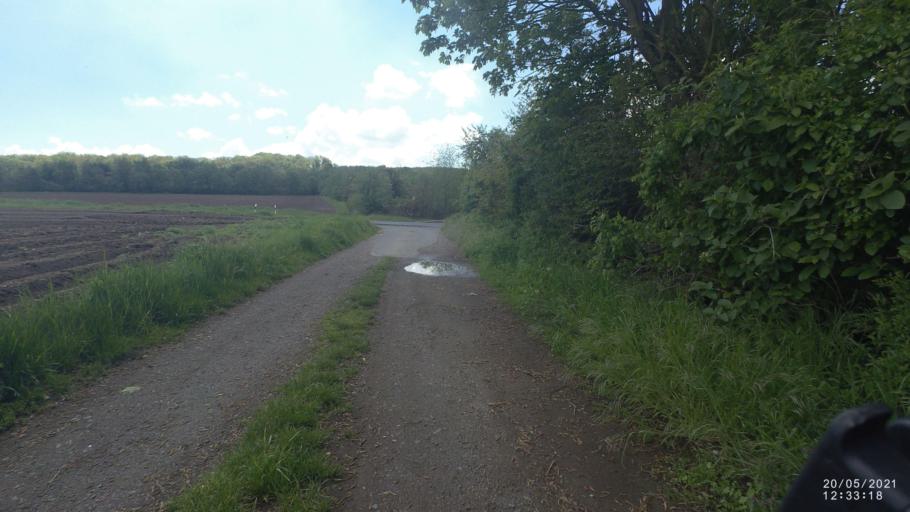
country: DE
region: Rheinland-Pfalz
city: Saffig
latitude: 50.3563
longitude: 7.4346
